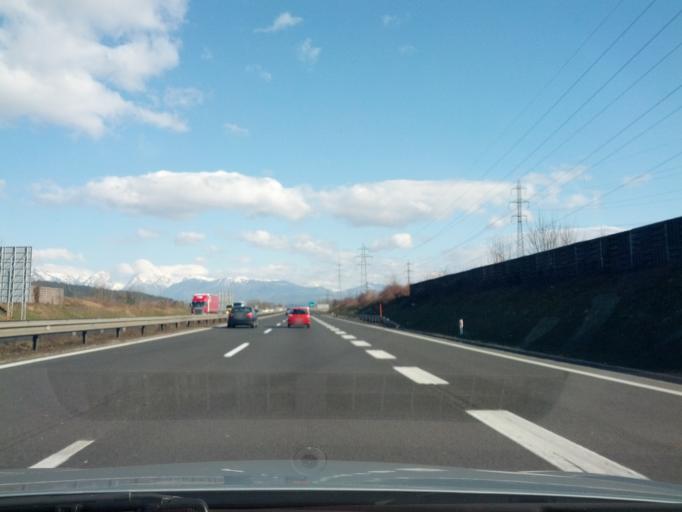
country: SI
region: Dol pri Ljubljani
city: Dol pri Ljubljani
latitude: 46.0763
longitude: 14.5803
